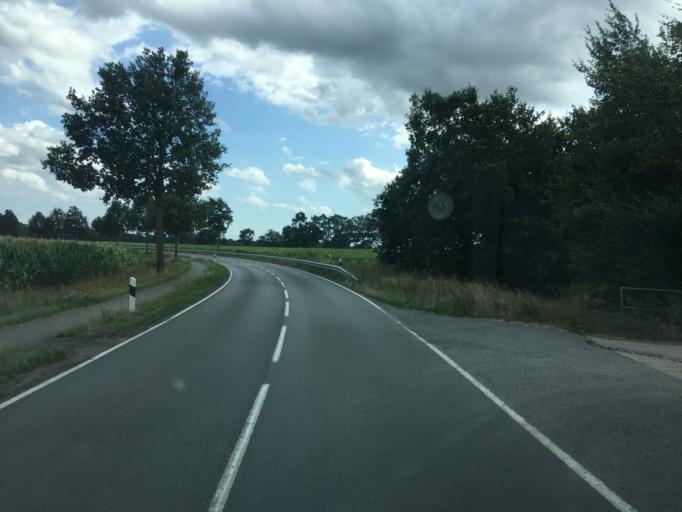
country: DE
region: Lower Saxony
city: Friesoythe
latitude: 53.0620
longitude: 7.8479
